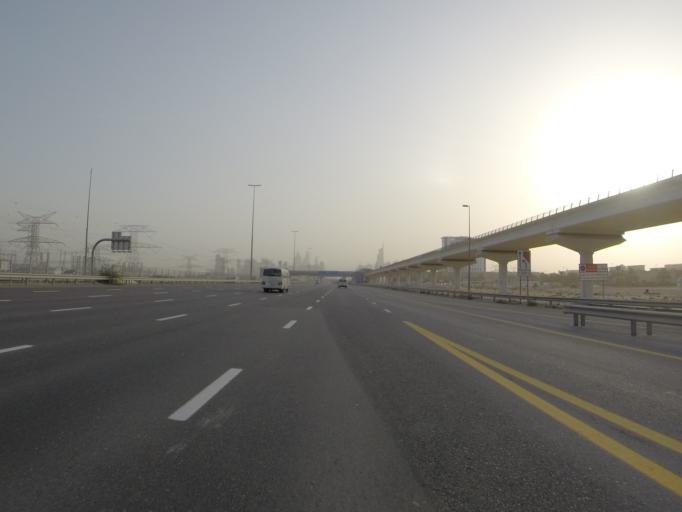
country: AE
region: Dubai
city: Dubai
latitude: 25.0425
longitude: 55.1134
